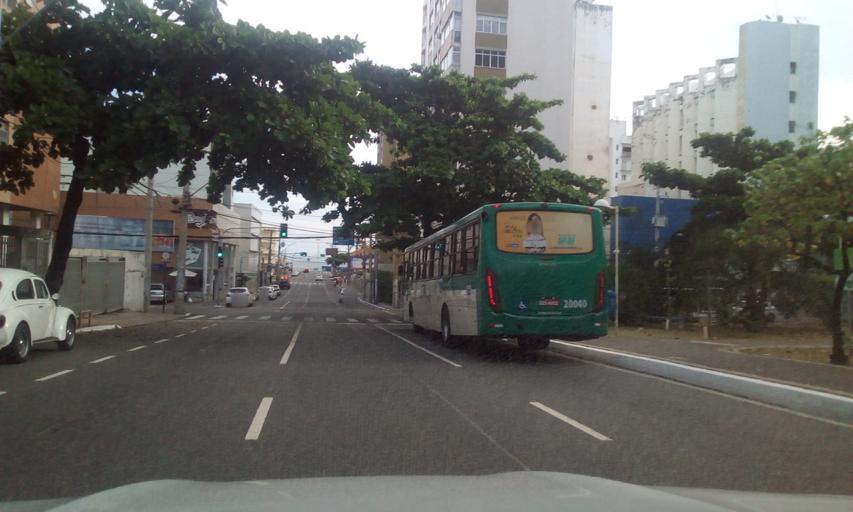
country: BR
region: Bahia
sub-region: Salvador
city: Salvador
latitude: -13.0039
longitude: -38.4589
